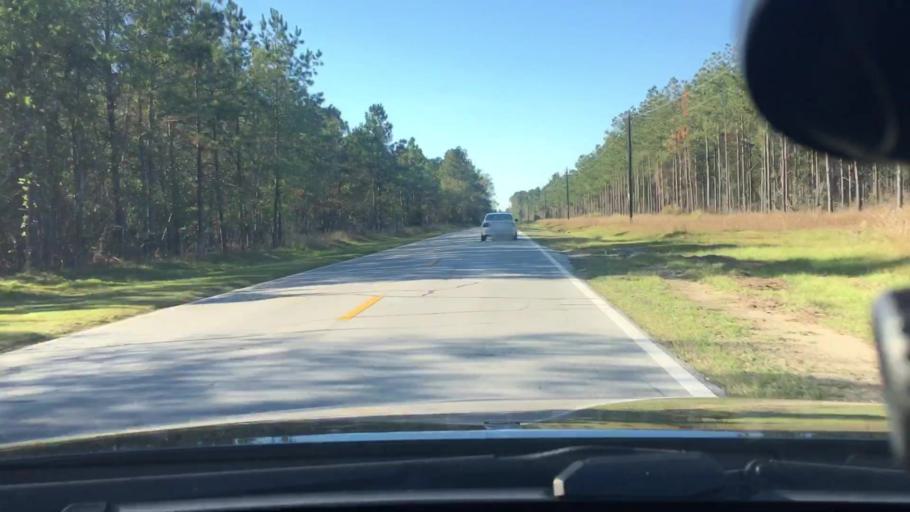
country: US
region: North Carolina
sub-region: Craven County
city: Vanceboro
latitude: 35.2231
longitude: -77.1281
